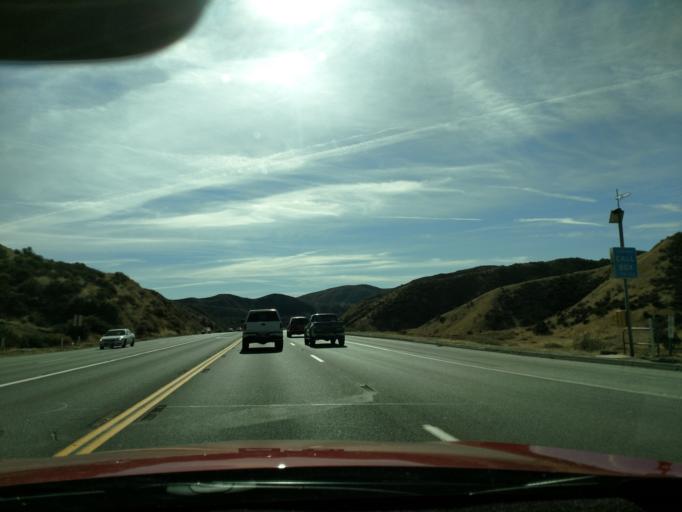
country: US
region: California
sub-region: Riverside County
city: Beaumont
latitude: 33.8831
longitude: -116.9909
